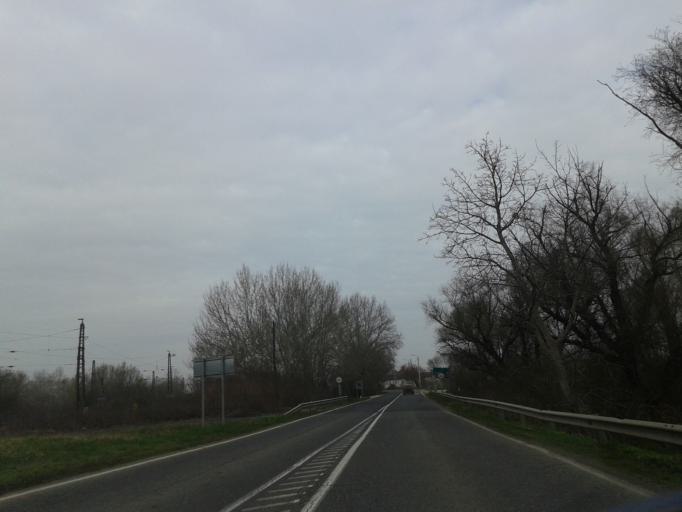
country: HU
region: Komarom-Esztergom
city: Almasfuzito
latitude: 47.7214
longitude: 18.2710
